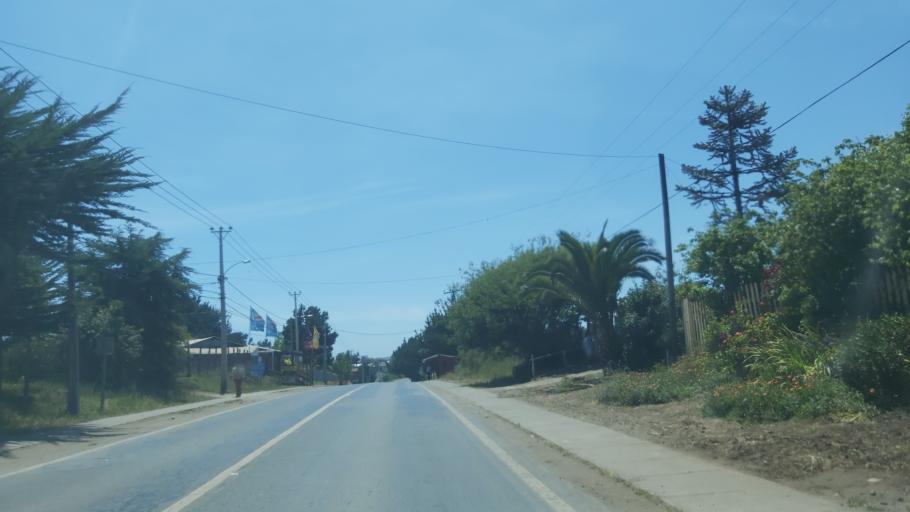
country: CL
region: Maule
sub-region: Provincia de Cauquenes
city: Cauquenes
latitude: -35.8020
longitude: -72.5654
